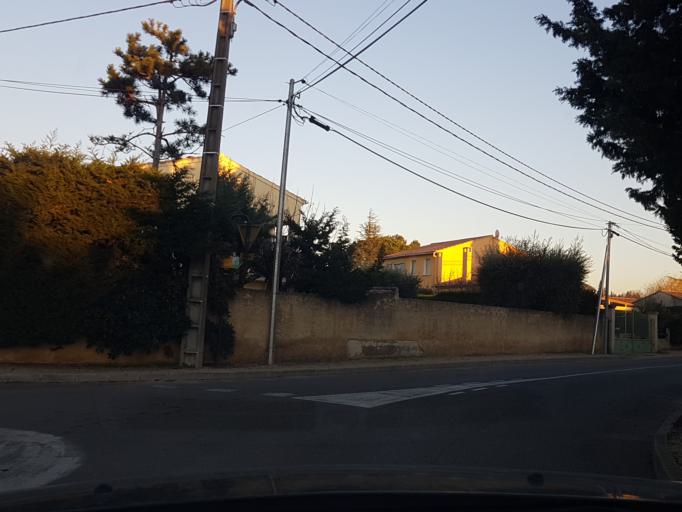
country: FR
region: Provence-Alpes-Cote d'Azur
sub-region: Departement du Vaucluse
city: Vedene
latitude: 43.9676
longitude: 4.9015
